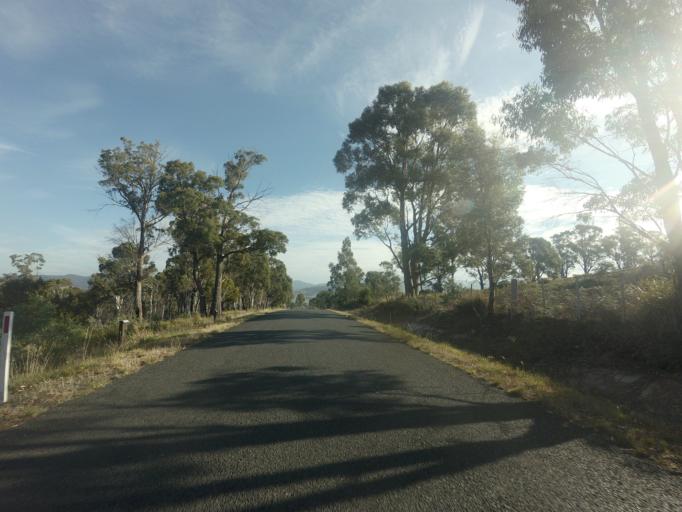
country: AU
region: Tasmania
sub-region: Brighton
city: Bridgewater
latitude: -42.5189
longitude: 147.3812
